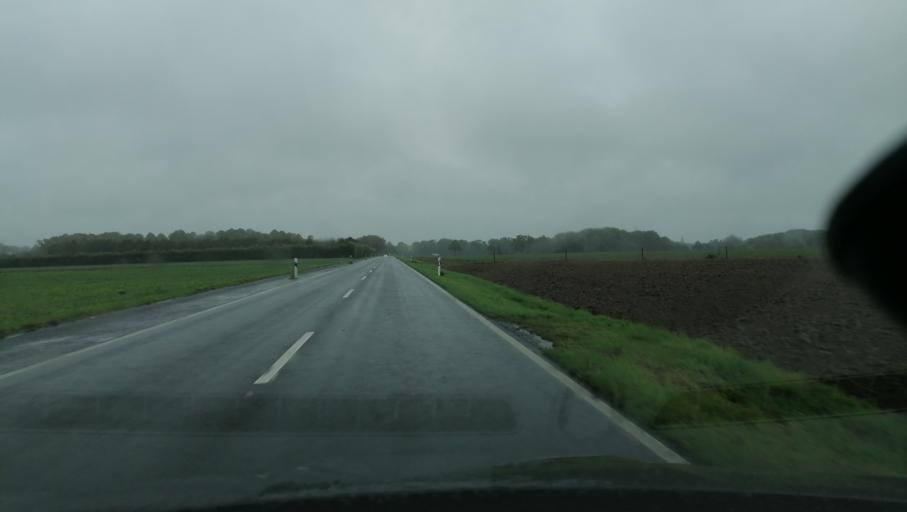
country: DE
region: North Rhine-Westphalia
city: Oer-Erkenschwick
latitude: 51.6239
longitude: 7.2914
